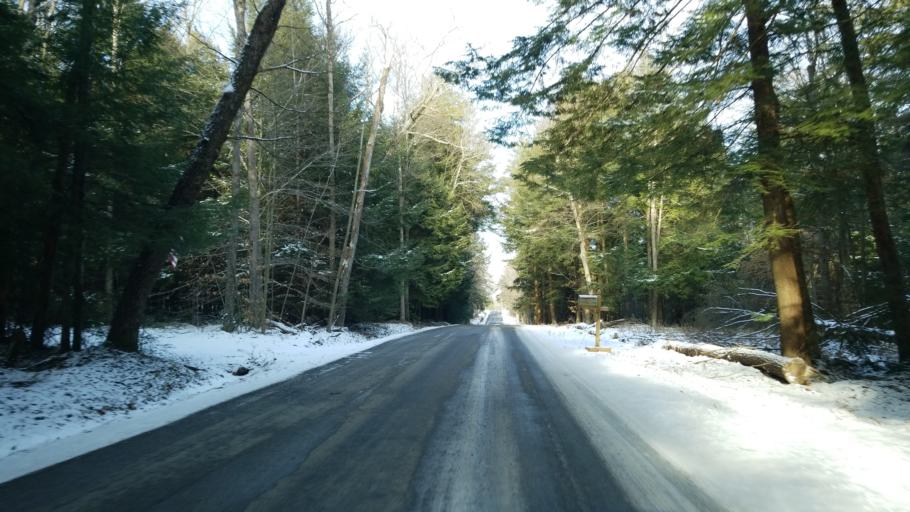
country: US
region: Pennsylvania
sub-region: Clearfield County
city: Treasure Lake
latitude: 41.0770
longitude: -78.6455
